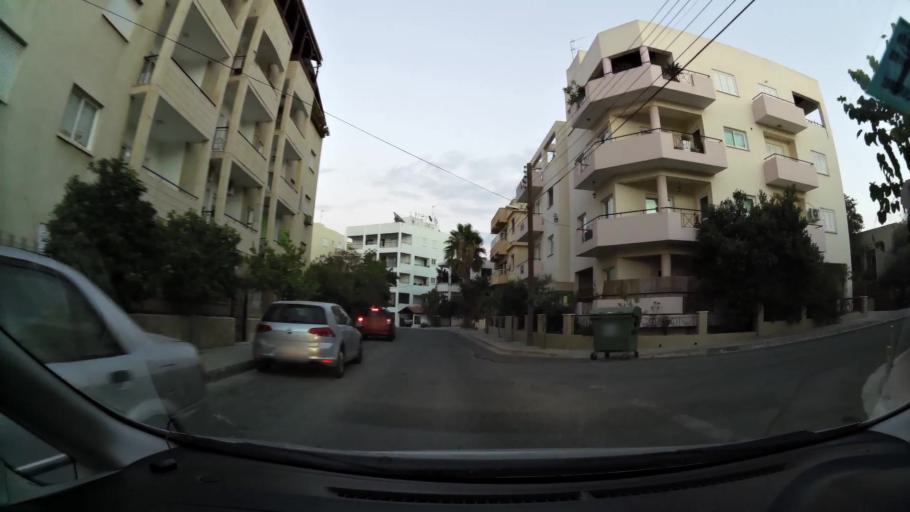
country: CY
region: Lefkosia
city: Nicosia
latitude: 35.1681
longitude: 33.3763
